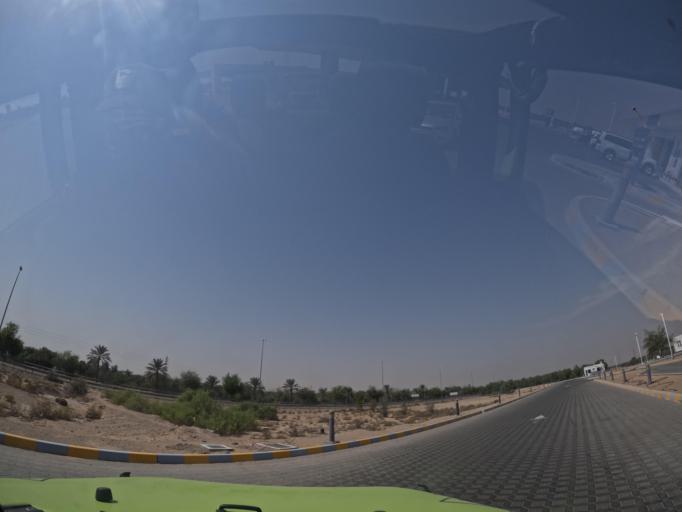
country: AE
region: Abu Dhabi
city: Al Ain
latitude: 24.1790
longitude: 55.1808
